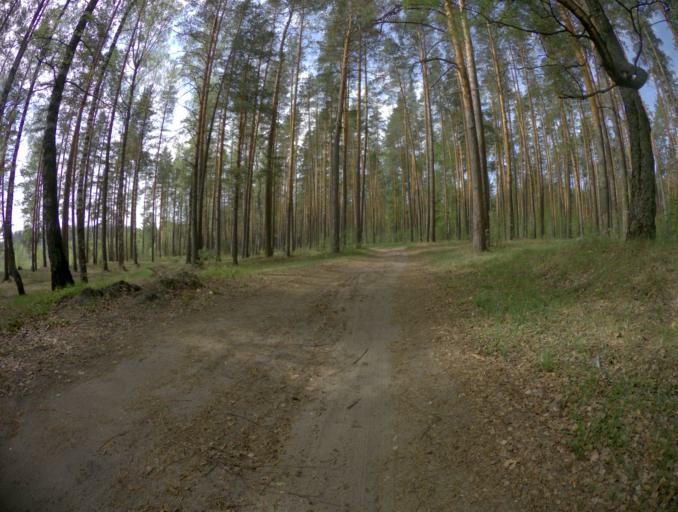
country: RU
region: Ivanovo
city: Yuzha
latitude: 56.5132
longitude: 42.1271
